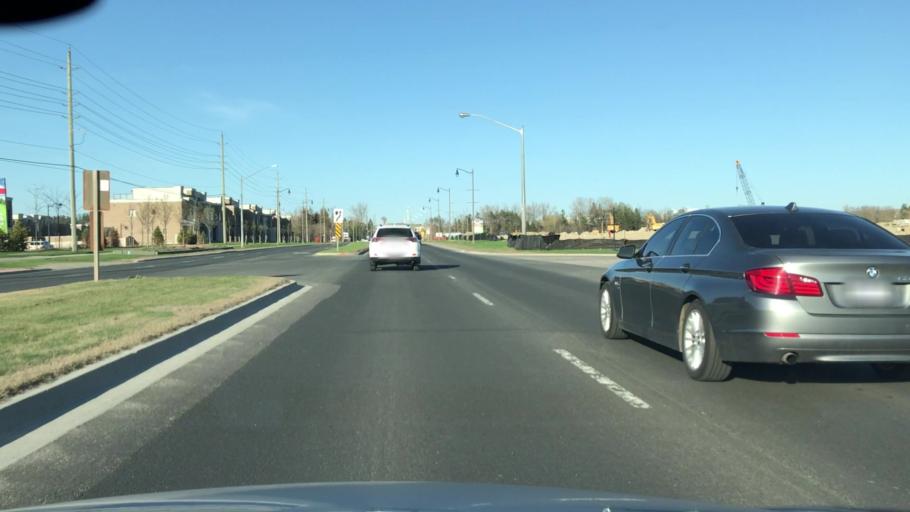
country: CA
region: Ontario
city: Newmarket
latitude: 44.0084
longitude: -79.4292
